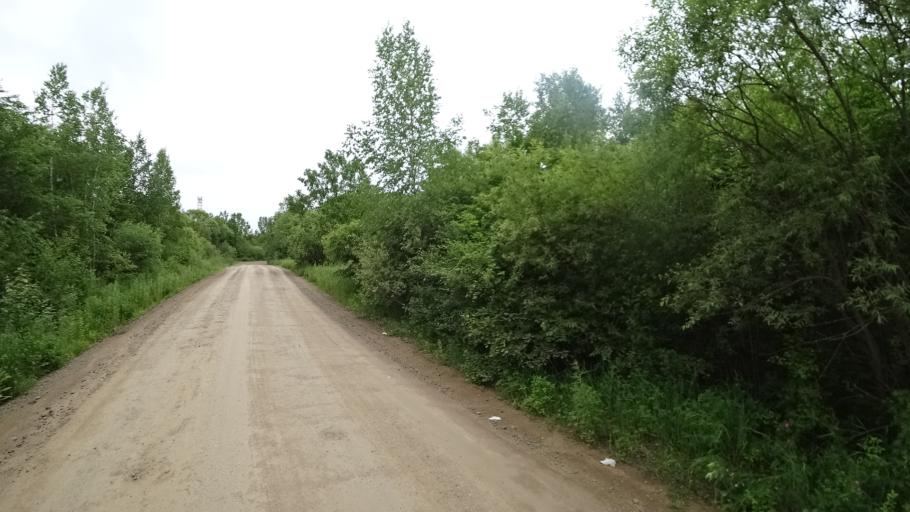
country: RU
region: Primorskiy
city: Arsen'yev
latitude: 44.1922
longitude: 133.3105
